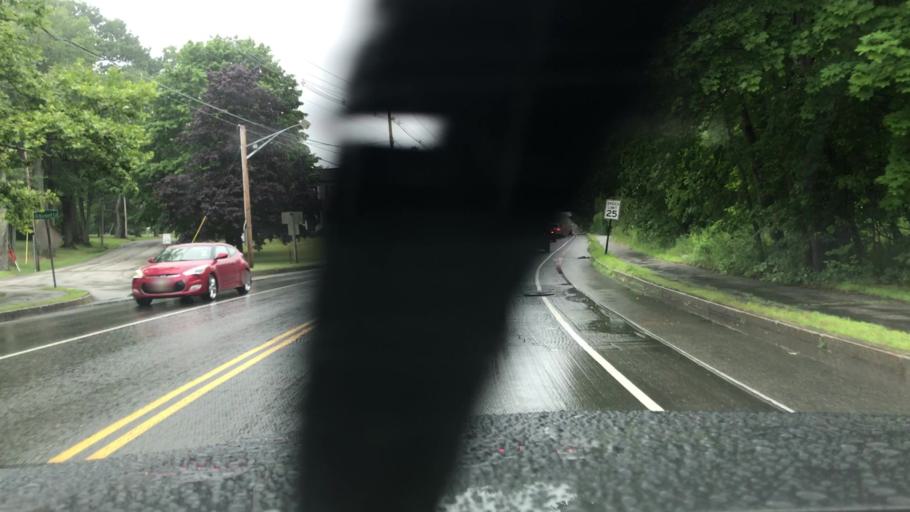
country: US
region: Maine
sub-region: York County
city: Kennebunk
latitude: 43.3887
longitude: -70.5367
